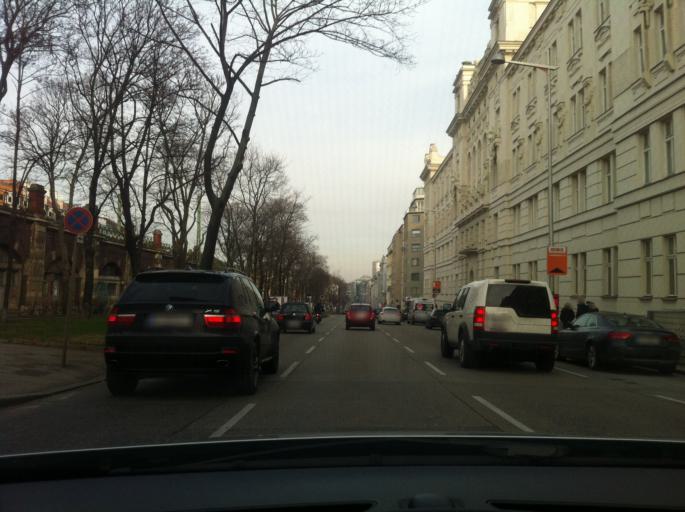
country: AT
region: Vienna
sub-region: Wien Stadt
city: Vienna
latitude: 48.2131
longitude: 16.3402
